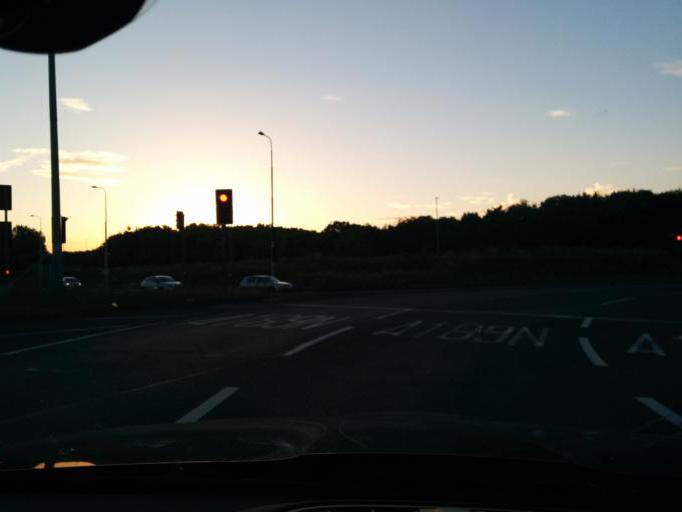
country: GB
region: England
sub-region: Northumberland
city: Cramlington
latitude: 55.0656
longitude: -1.5792
